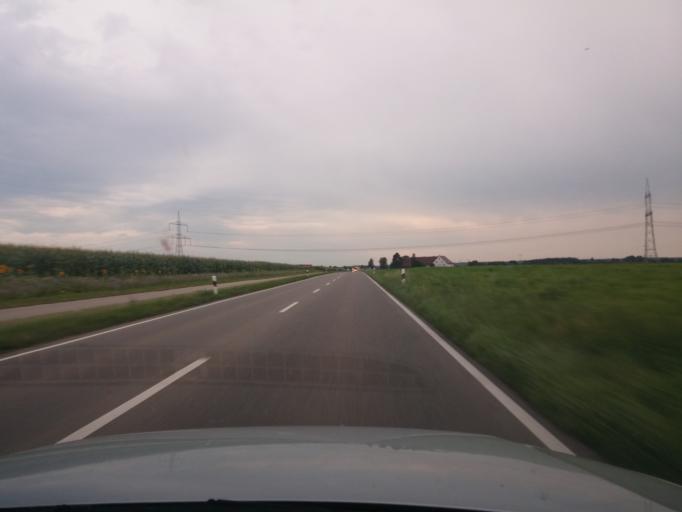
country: DE
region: Bavaria
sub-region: Swabia
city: Buxheim
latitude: 47.9690
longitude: 10.1439
